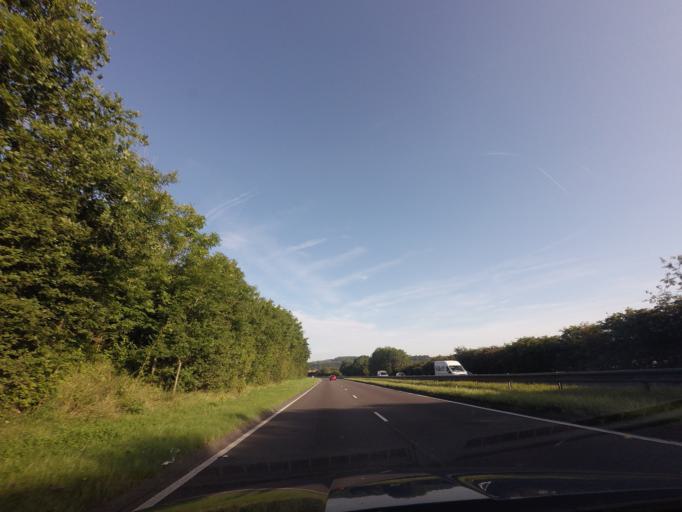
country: GB
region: England
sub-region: Derbyshire
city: Chesterfield
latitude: 53.2208
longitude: -1.3983
